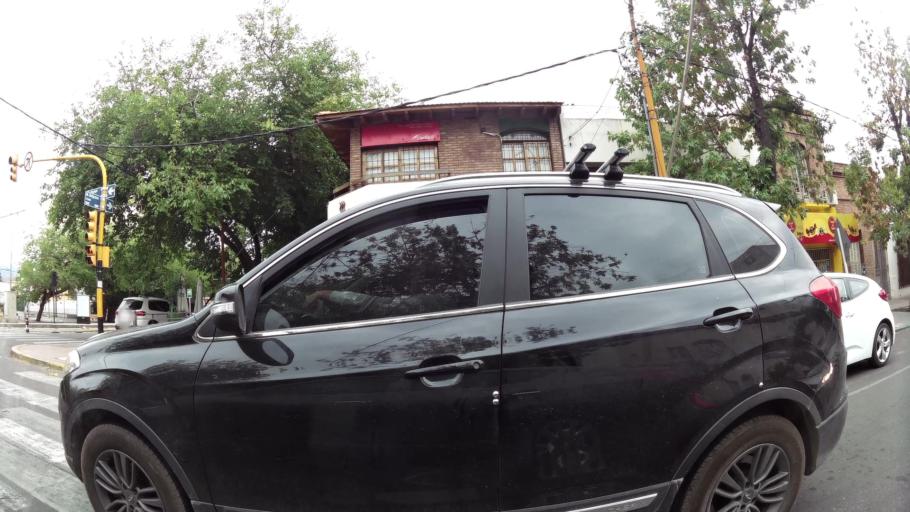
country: AR
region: Mendoza
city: Mendoza
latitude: -32.8876
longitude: -68.8507
